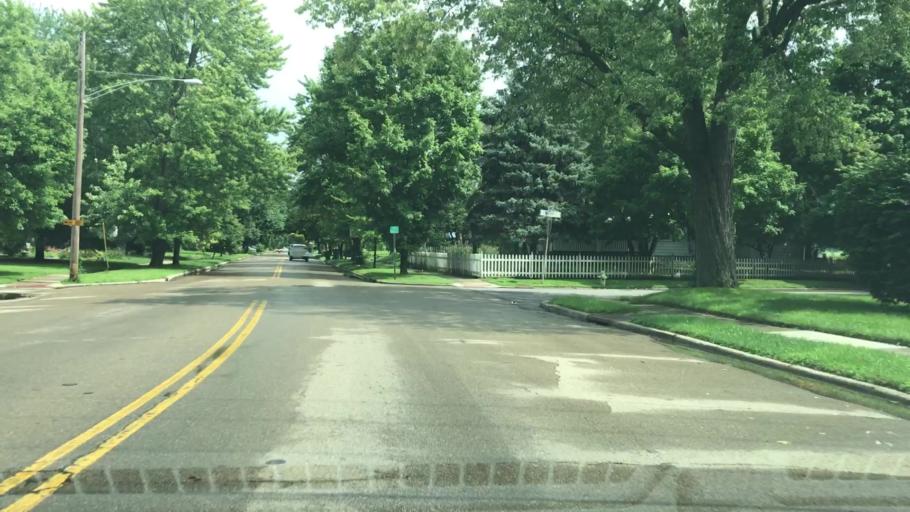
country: US
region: Ohio
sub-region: Greene County
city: Fairborn
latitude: 39.8245
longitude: -84.0238
